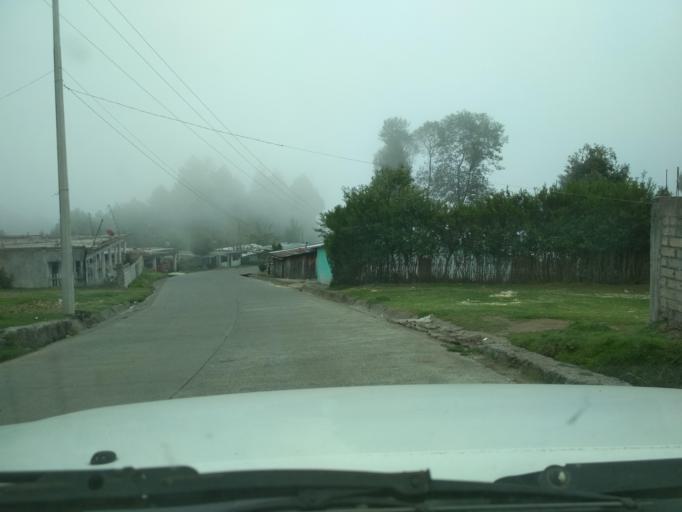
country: MX
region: Veracruz
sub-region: La Perla
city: Chilapa
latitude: 18.9761
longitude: -97.2002
